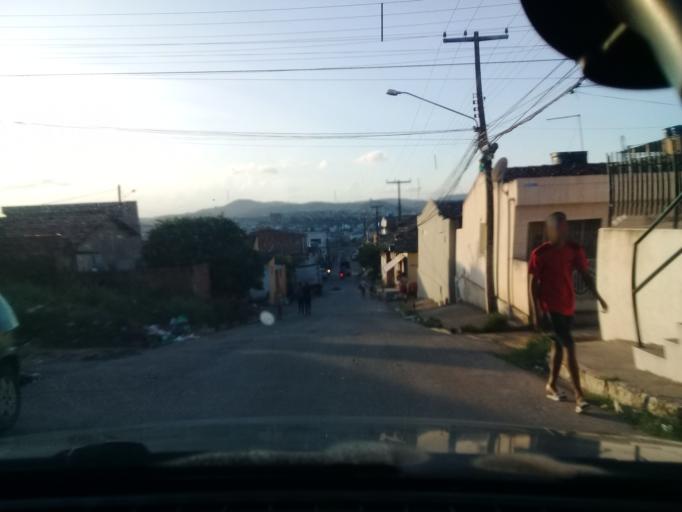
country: BR
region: Pernambuco
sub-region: Vitoria De Santo Antao
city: Vitoria de Santo Antao
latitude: -8.1304
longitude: -35.2893
